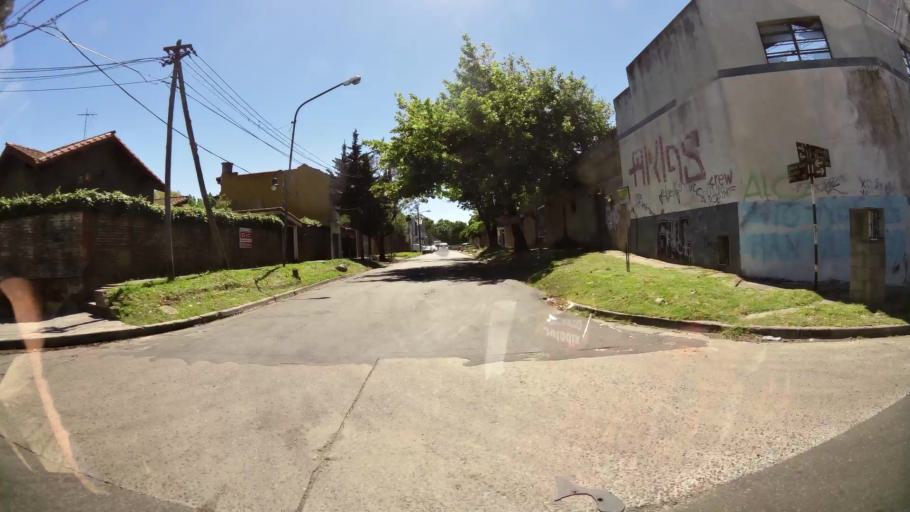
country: AR
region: Buenos Aires
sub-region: Partido de General San Martin
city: General San Martin
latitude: -34.5422
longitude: -58.5373
